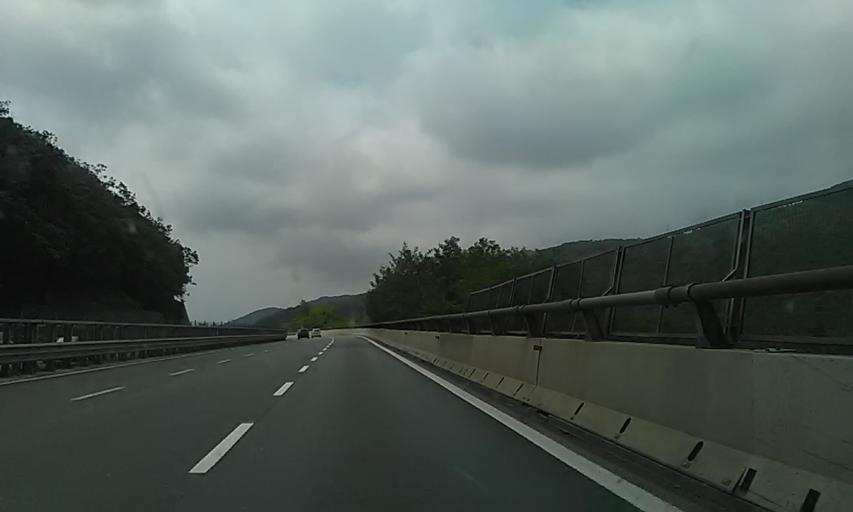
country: IT
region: Liguria
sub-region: Provincia di Genova
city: Masone
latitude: 44.4772
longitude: 8.7353
